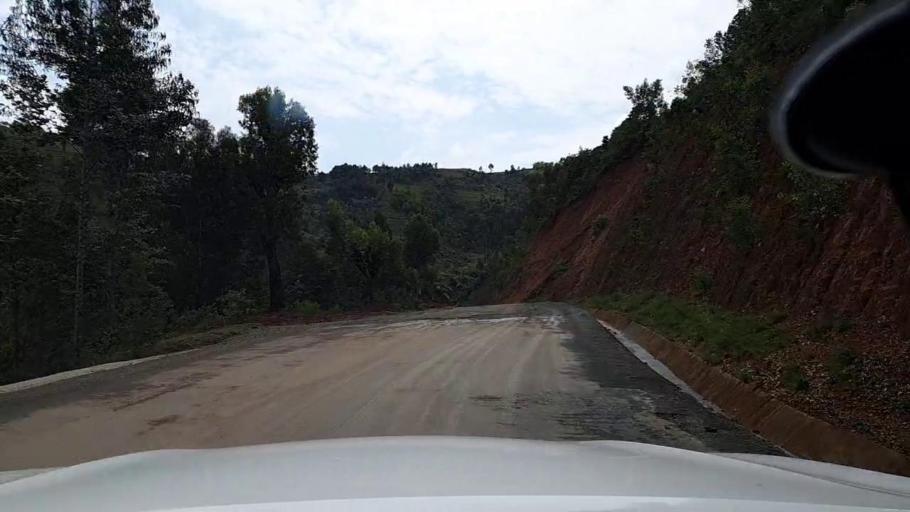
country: RW
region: Southern Province
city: Gitarama
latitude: -2.0628
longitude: 29.5608
